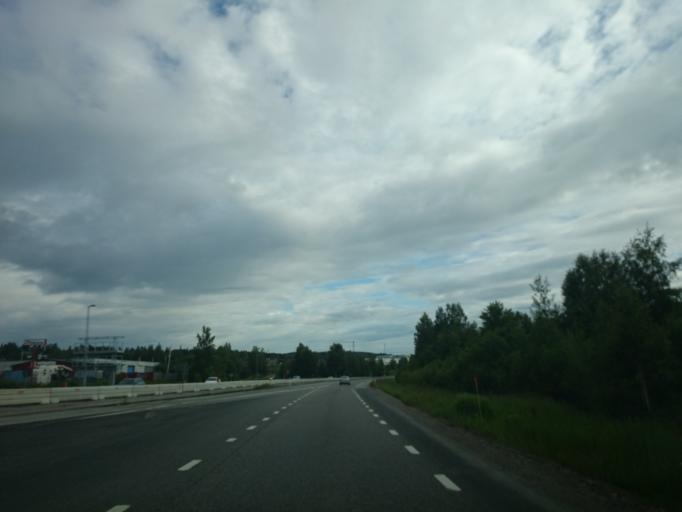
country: SE
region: Vaesternorrland
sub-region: Sundsvalls Kommun
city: Sundsvall
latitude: 62.4066
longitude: 17.3373
